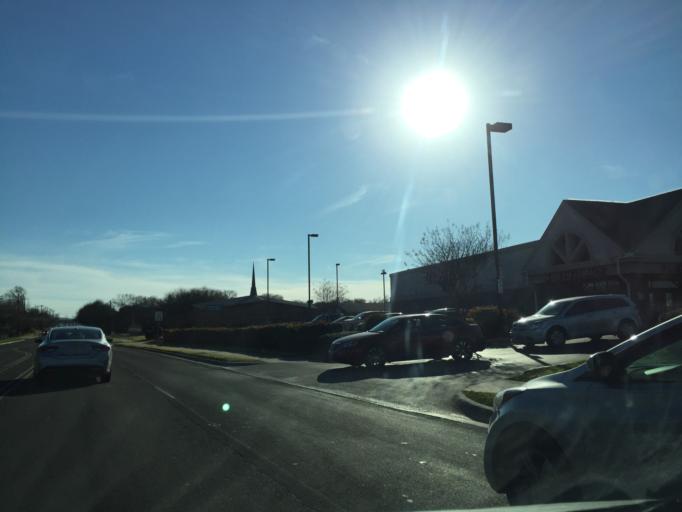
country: US
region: Texas
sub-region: Travis County
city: Rollingwood
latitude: 30.2083
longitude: -97.7817
